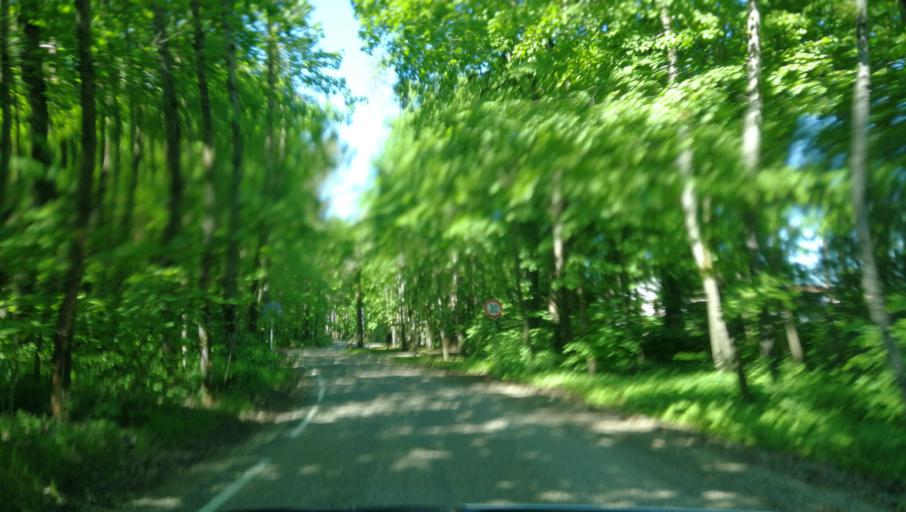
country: LV
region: Kekava
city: Kekava
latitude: 56.8649
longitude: 24.2420
